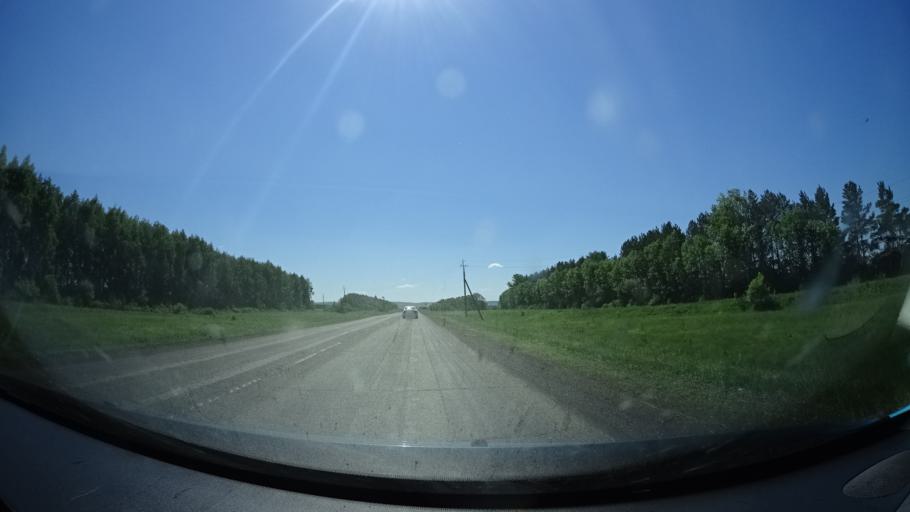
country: RU
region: Bashkortostan
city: Blagoveshchensk
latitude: 55.2302
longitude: 55.7842
